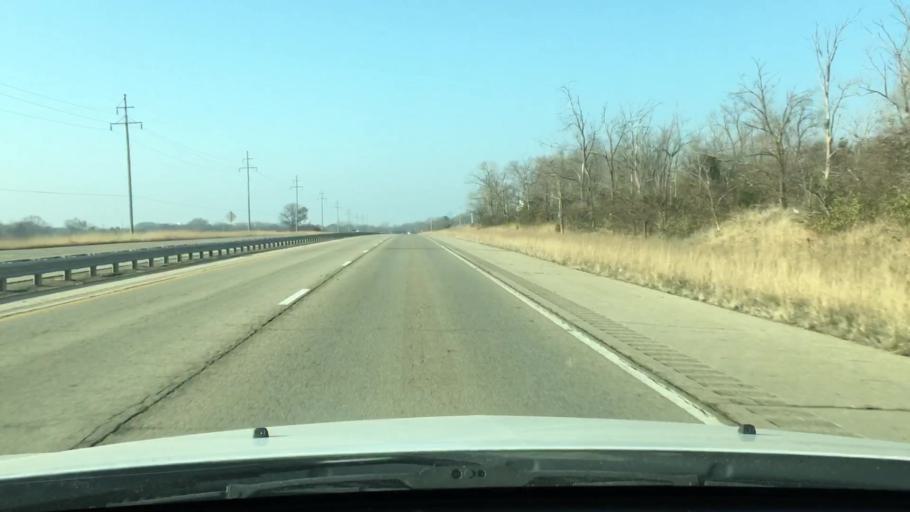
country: US
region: Illinois
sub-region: Tazewell County
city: Pekin
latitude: 40.5790
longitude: -89.7001
